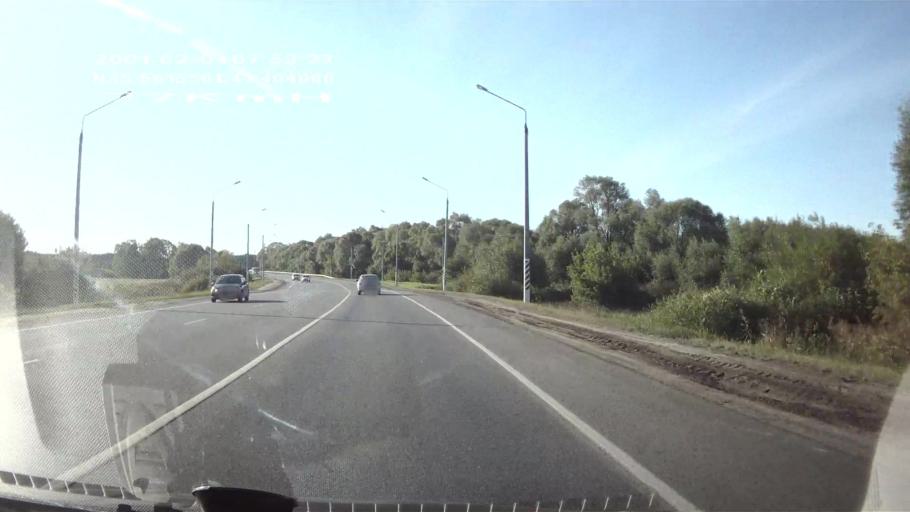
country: RU
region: Chuvashia
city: Shikhazany
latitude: 55.5613
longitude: 47.4043
